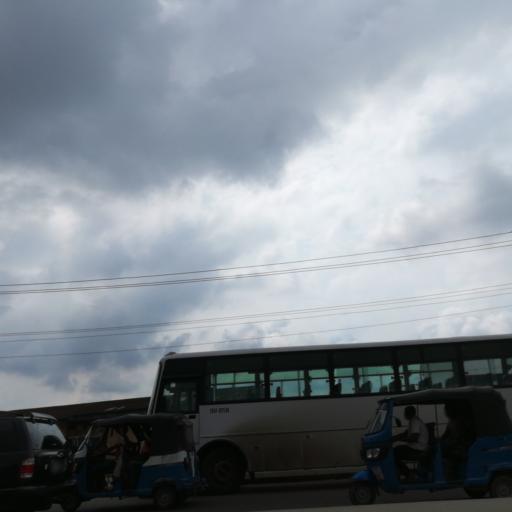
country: NG
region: Rivers
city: Port Harcourt
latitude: 4.8293
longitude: 7.0708
